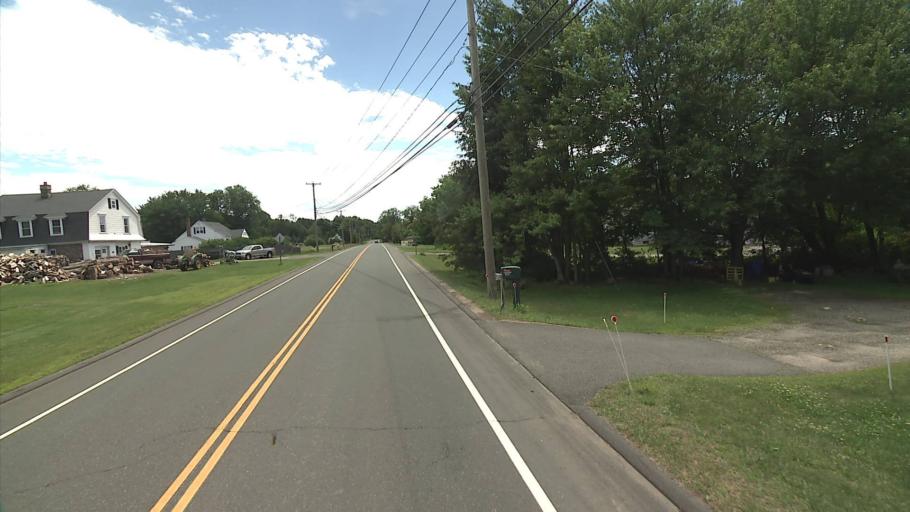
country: US
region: Connecticut
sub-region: Litchfield County
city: Watertown
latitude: 41.6325
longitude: -73.1394
